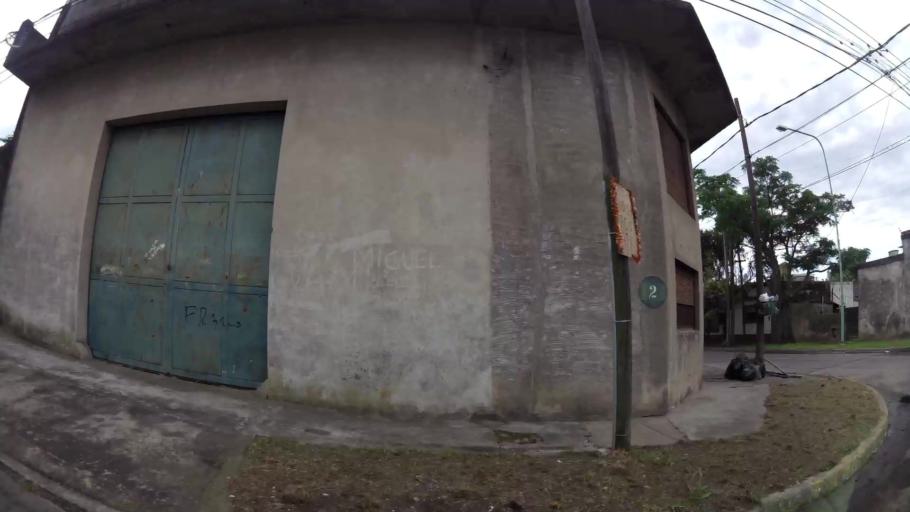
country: AR
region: Buenos Aires
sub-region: Partido de Quilmes
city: Quilmes
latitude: -34.7530
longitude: -58.2234
